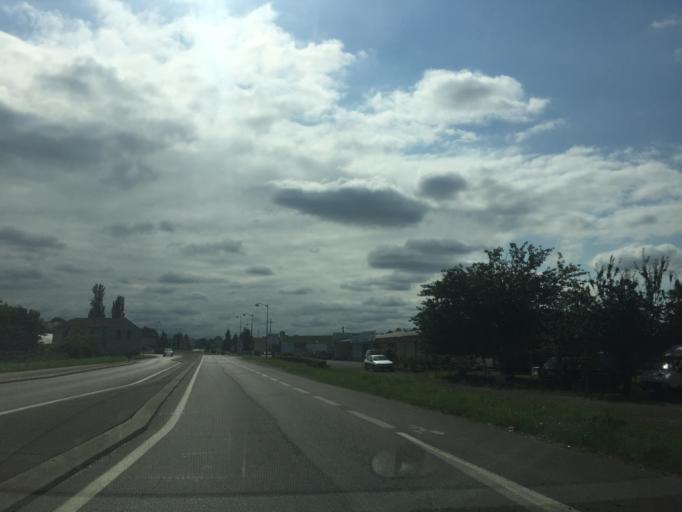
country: FR
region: Midi-Pyrenees
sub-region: Departement de la Haute-Garonne
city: Saint-Gaudens
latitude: 43.0965
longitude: 0.7044
